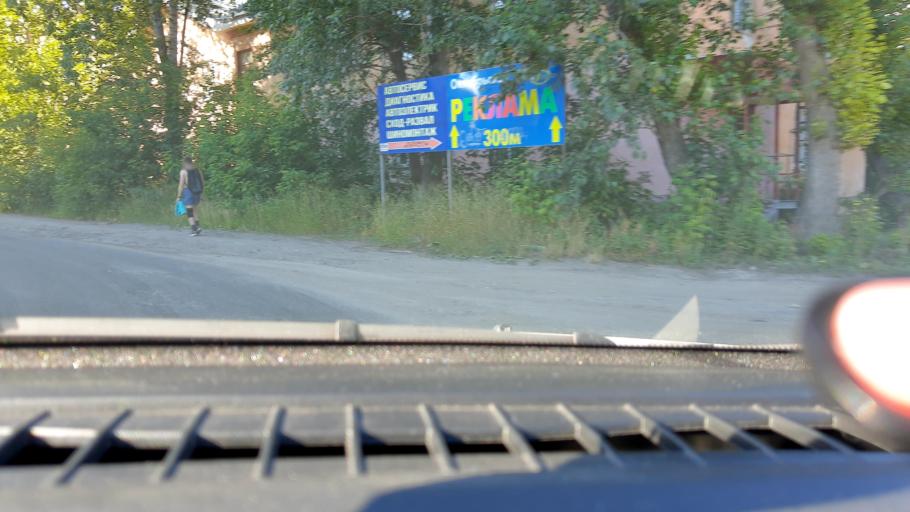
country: RU
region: Nizjnij Novgorod
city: Dzerzhinsk
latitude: 56.2374
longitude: 43.4909
